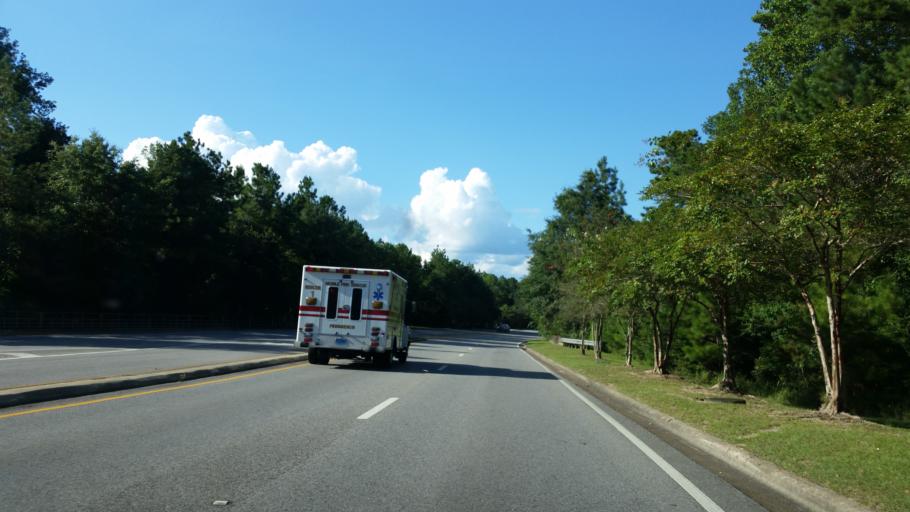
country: US
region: Alabama
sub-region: Mobile County
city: Prichard
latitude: 30.7045
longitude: -88.1741
